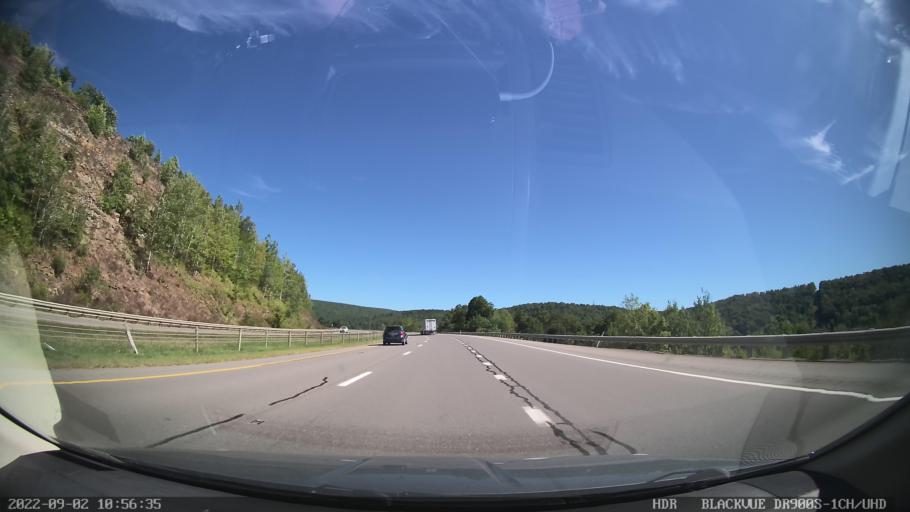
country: US
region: Pennsylvania
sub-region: Tioga County
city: Blossburg
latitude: 41.6784
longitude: -77.0702
